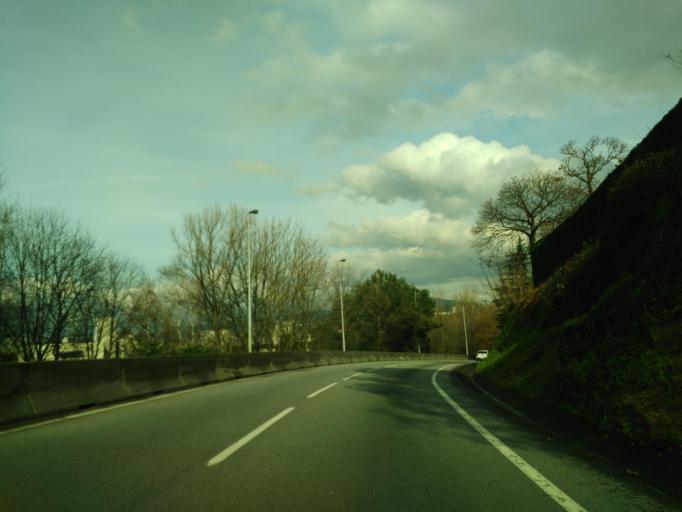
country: PT
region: Braga
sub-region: Guimaraes
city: Guimaraes
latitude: 41.4448
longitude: -8.3089
